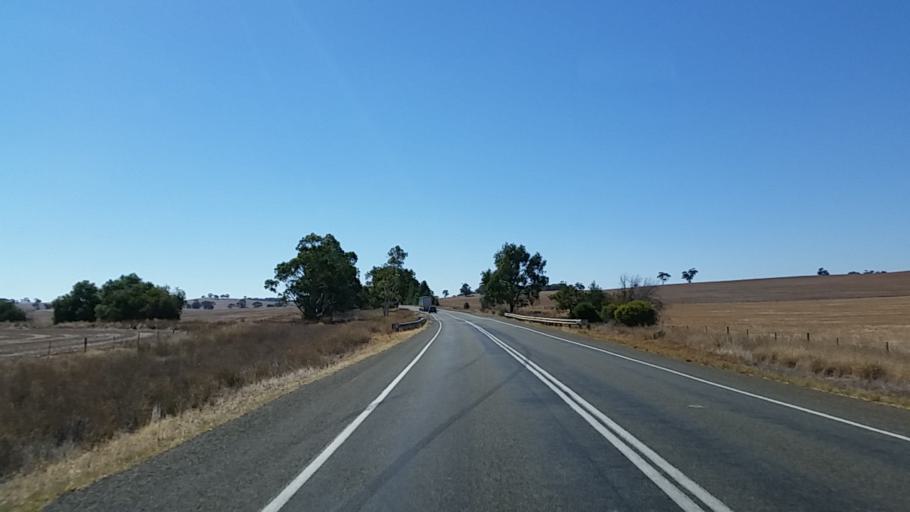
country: AU
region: South Australia
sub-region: Clare and Gilbert Valleys
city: Clare
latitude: -34.0585
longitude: 138.7944
